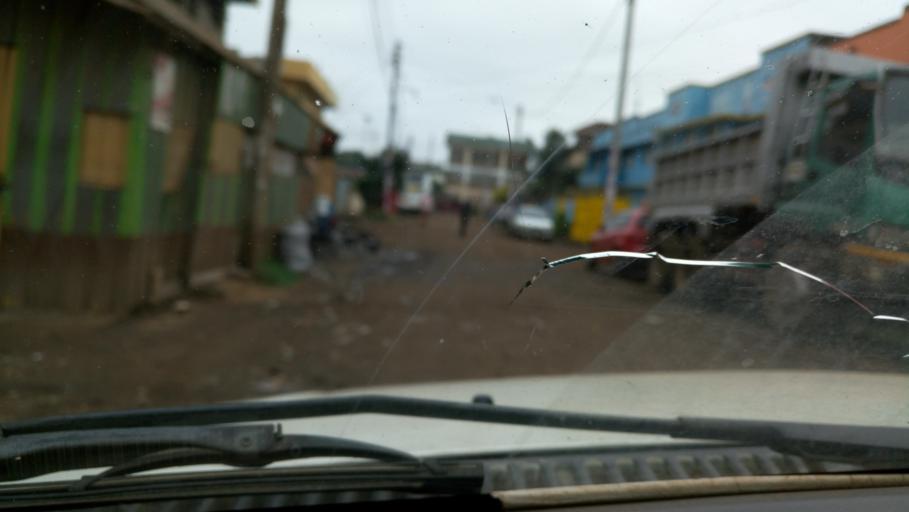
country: KE
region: Nairobi Area
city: Nairobi
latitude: -1.2727
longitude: 36.8327
